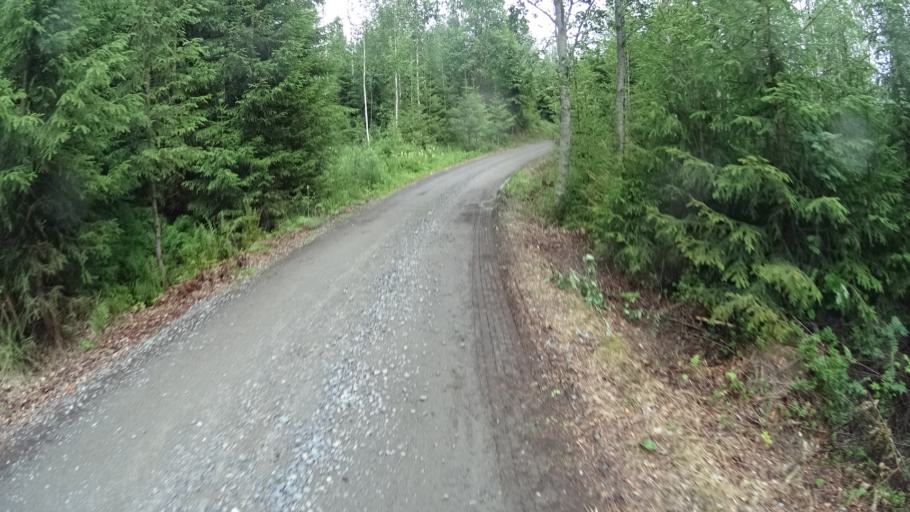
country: FI
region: Uusimaa
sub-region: Helsinki
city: Karkkila
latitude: 60.5809
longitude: 24.2831
